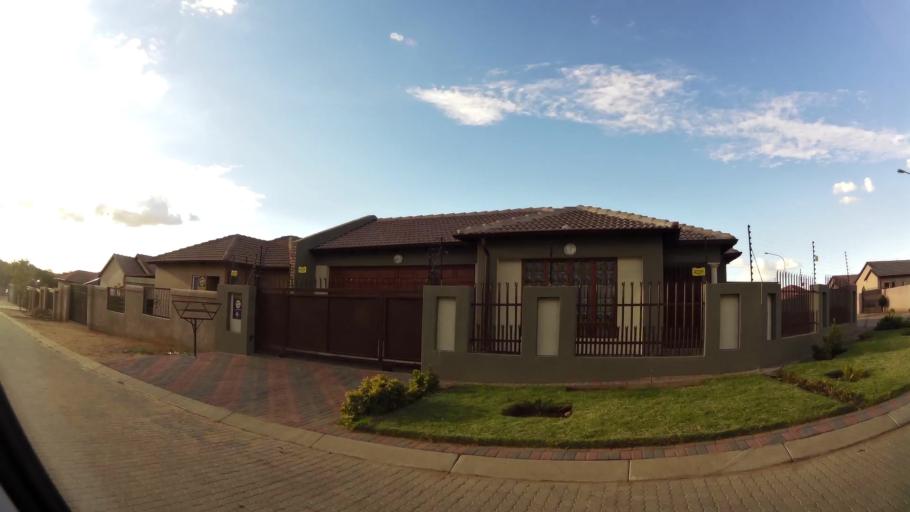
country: ZA
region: Limpopo
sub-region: Capricorn District Municipality
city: Polokwane
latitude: -23.9262
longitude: 29.4173
